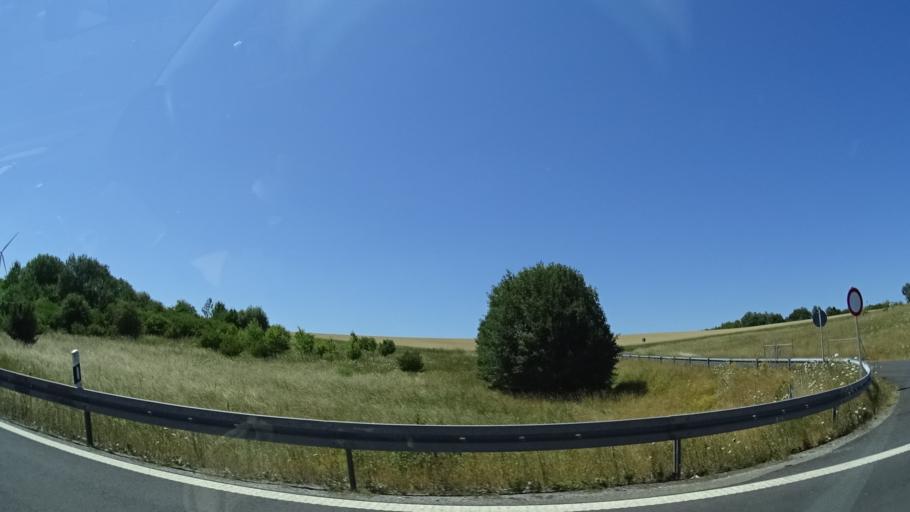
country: DE
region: Bavaria
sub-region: Regierungsbezirk Unterfranken
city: Munnerstadt
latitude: 50.2426
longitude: 10.2172
